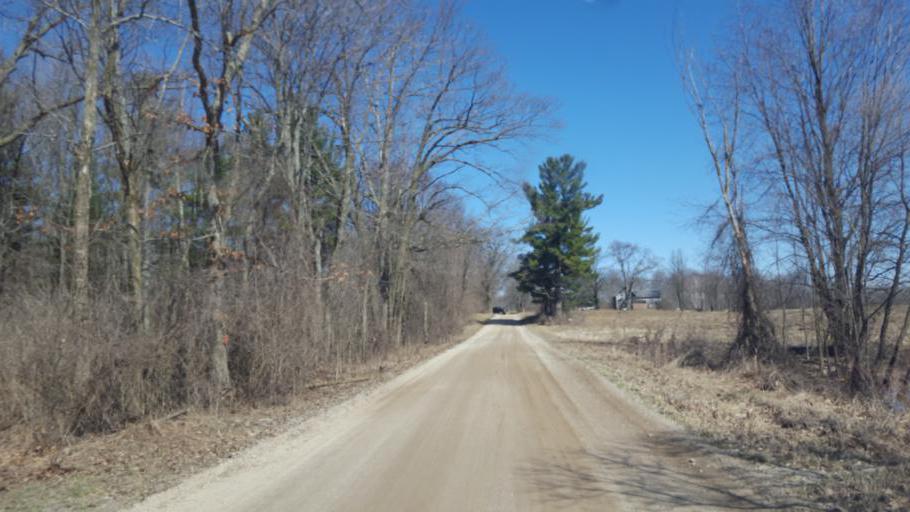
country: US
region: Michigan
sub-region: Montcalm County
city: Edmore
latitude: 43.4549
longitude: -85.0850
